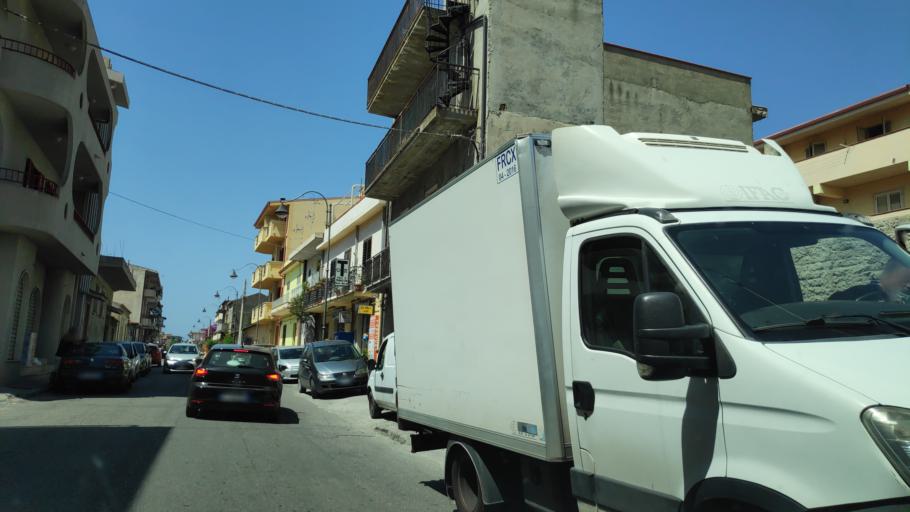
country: IT
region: Calabria
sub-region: Provincia di Reggio Calabria
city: Bova Marina
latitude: 37.9302
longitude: 15.9151
